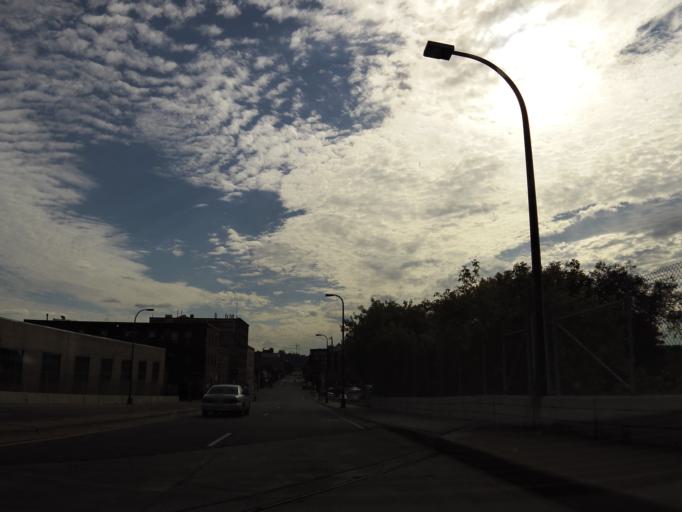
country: US
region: Minnesota
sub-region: Hennepin County
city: Minneapolis
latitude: 44.9925
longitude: -93.2505
